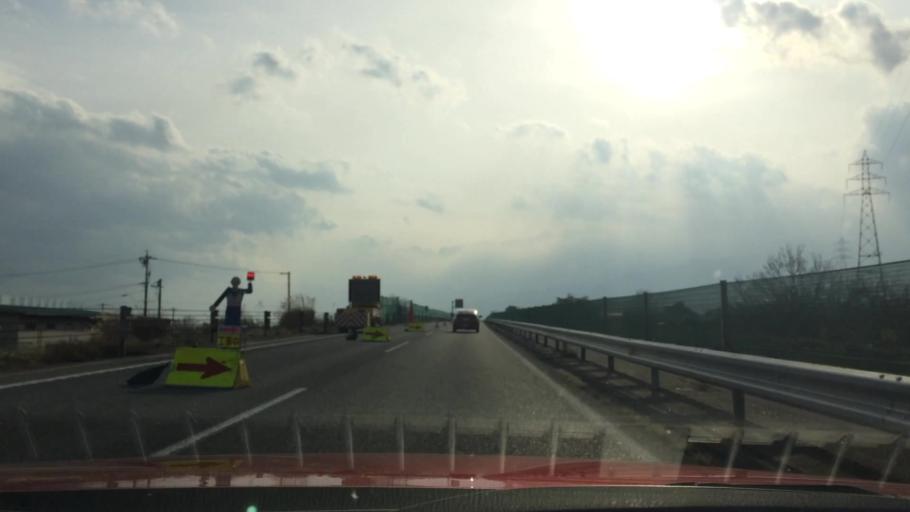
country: JP
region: Nagano
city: Tatsuno
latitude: 35.9183
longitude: 137.9687
